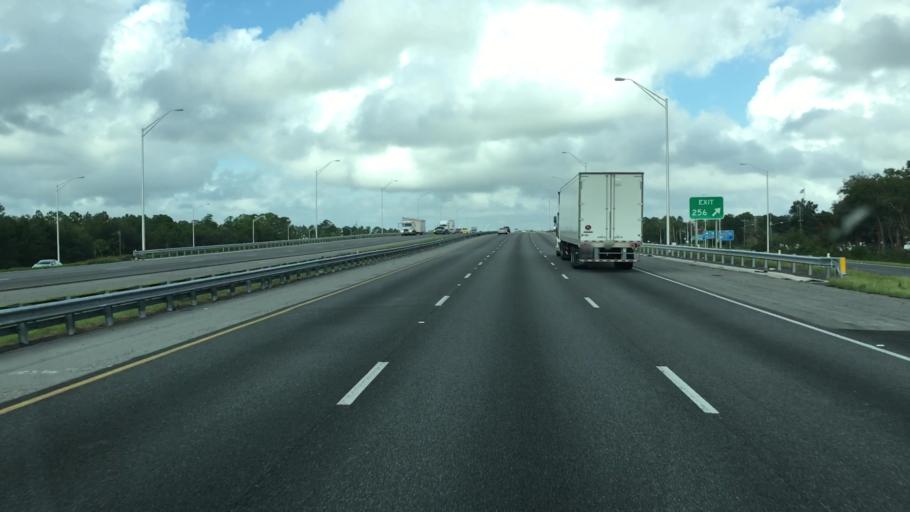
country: US
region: Florida
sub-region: Volusia County
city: Port Orange
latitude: 29.1023
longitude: -81.0267
